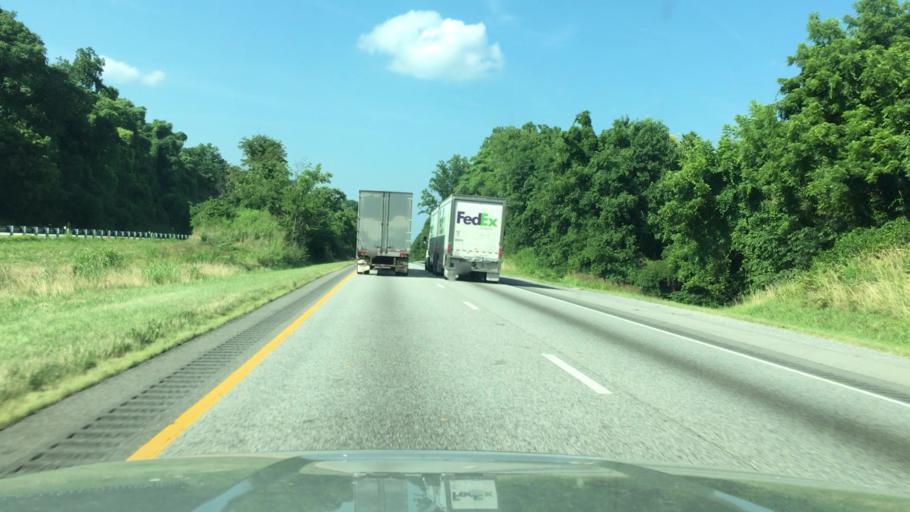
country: US
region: Virginia
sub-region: Botetourt County
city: Daleville
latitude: 37.4204
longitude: -79.8822
